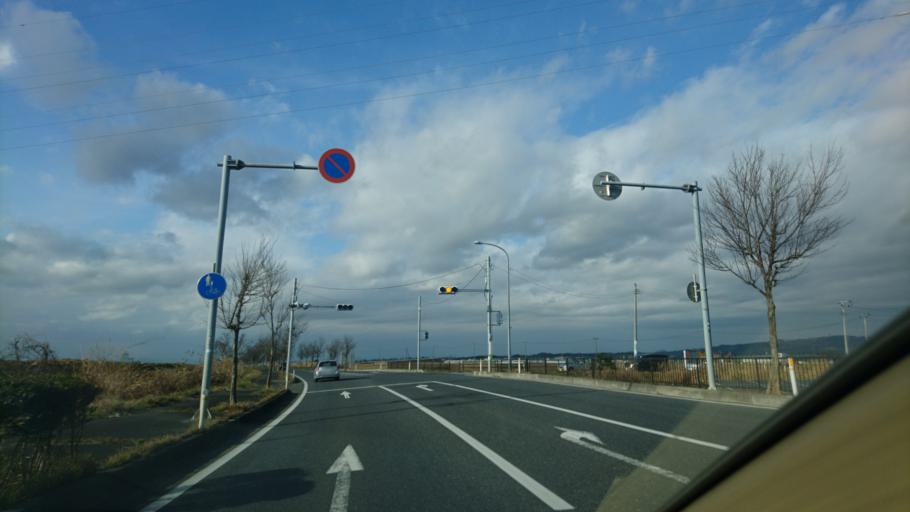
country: JP
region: Miyagi
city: Wakuya
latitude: 38.5375
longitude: 141.1174
